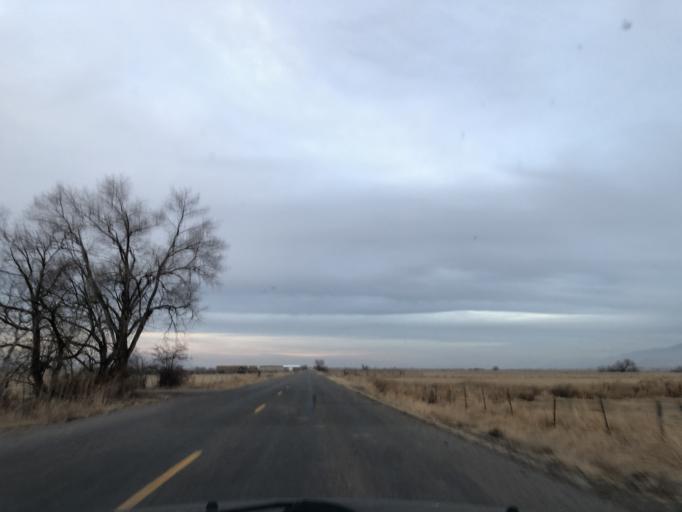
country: US
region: Utah
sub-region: Cache County
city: Benson
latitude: 41.7468
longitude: -111.9117
